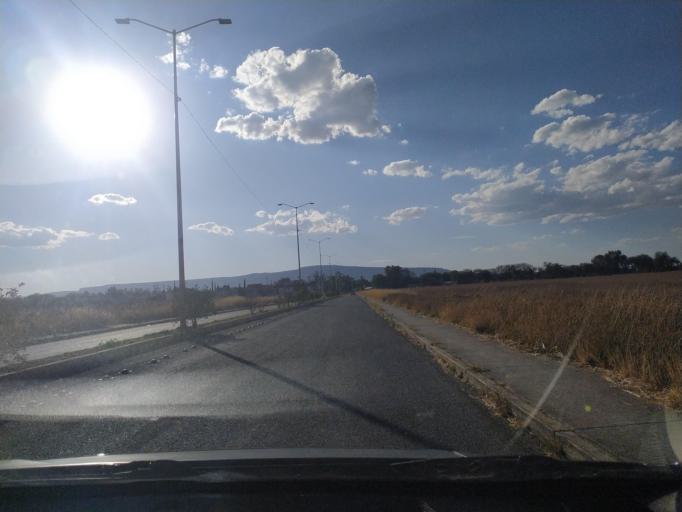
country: MX
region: Guanajuato
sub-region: San Francisco del Rincon
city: Fraccionamiento la Mezquitera
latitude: 21.0118
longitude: -101.8317
